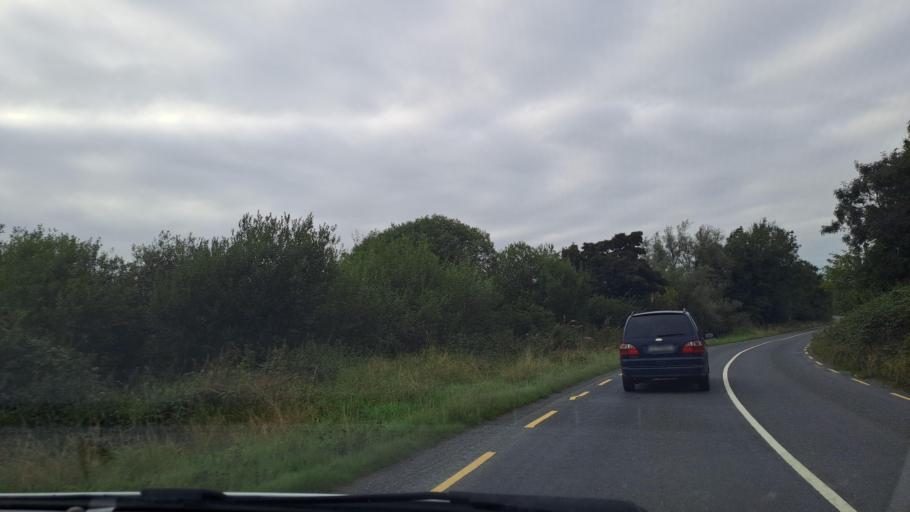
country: IE
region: Ulster
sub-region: County Monaghan
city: Carrickmacross
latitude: 54.0115
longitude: -6.7559
